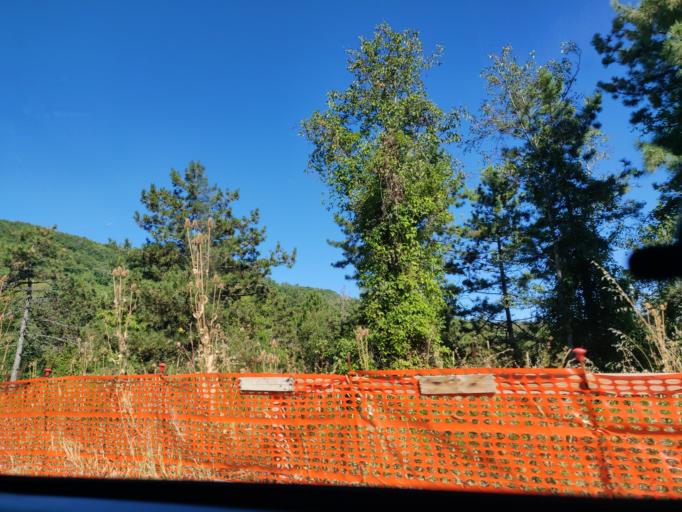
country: IT
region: Tuscany
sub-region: Provincia di Siena
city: Piancastagnaio
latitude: 42.8602
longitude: 11.6793
